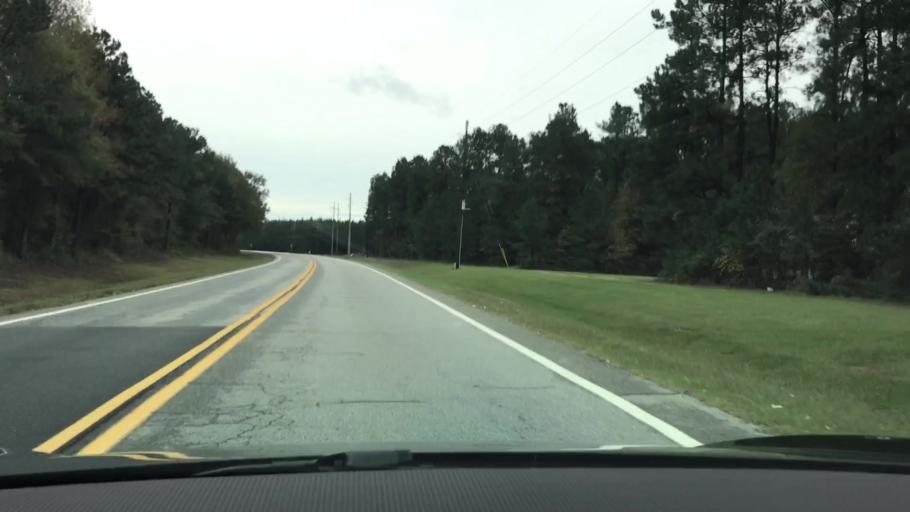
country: US
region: Georgia
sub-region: Warren County
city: Warrenton
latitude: 33.3926
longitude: -82.6485
